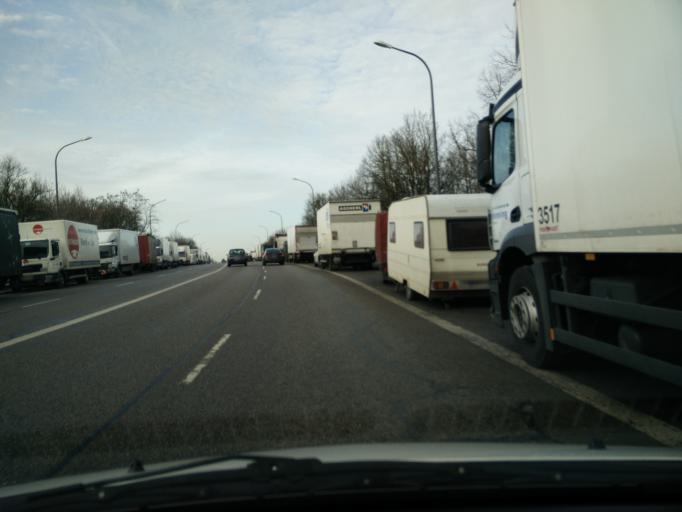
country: DE
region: Bavaria
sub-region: Upper Bavaria
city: Karlsfeld
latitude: 48.1743
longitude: 11.5024
